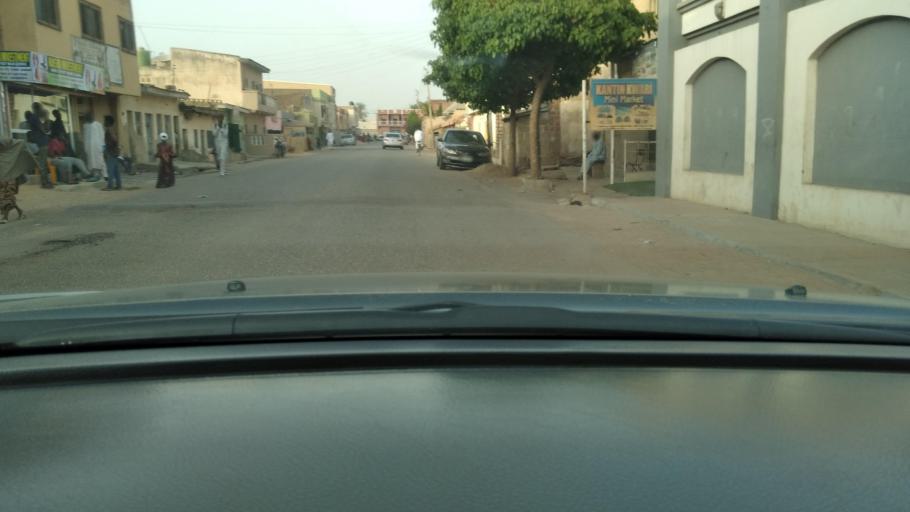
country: NG
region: Kano
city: Kano
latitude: 11.9592
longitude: 8.5243
